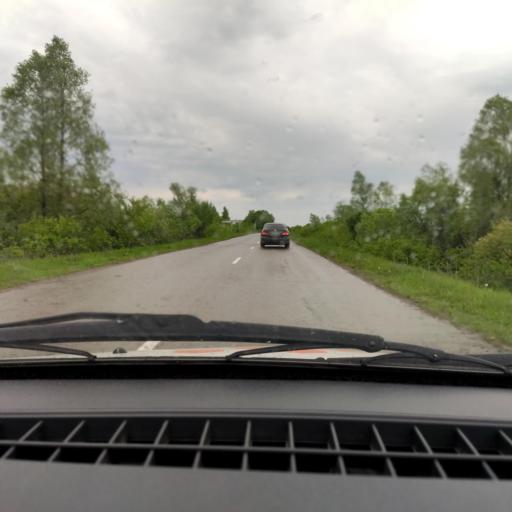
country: RU
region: Bashkortostan
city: Kudeyevskiy
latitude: 54.8324
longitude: 56.7929
